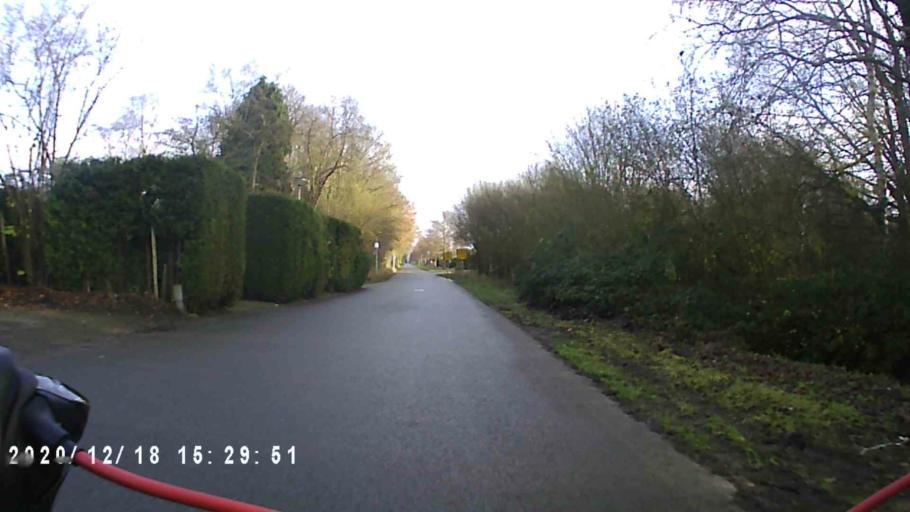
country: NL
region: Groningen
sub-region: Gemeente Hoogezand-Sappemeer
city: Hoogezand
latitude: 53.1440
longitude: 6.7106
